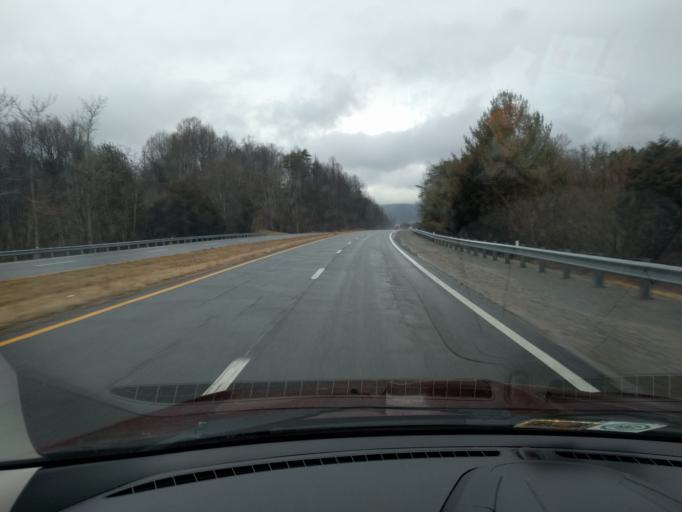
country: US
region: Virginia
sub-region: Montgomery County
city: Prices Fork
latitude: 37.2932
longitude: -80.5012
